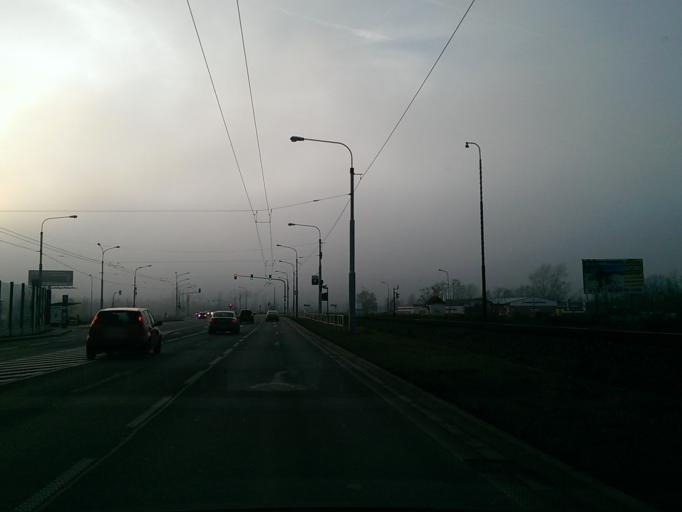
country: CZ
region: Zlin
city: Tecovice
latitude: 49.2069
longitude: 17.5814
